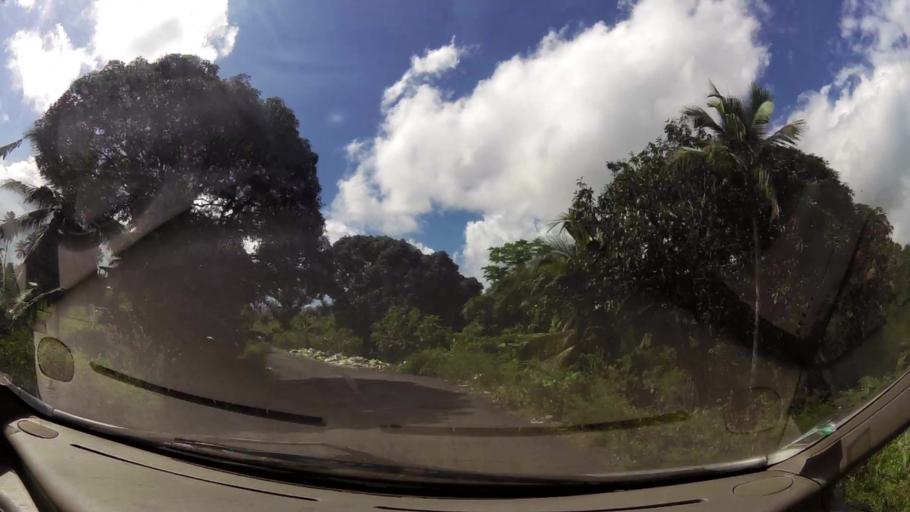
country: KM
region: Grande Comore
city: Mavingouni
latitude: -11.7406
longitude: 43.2457
